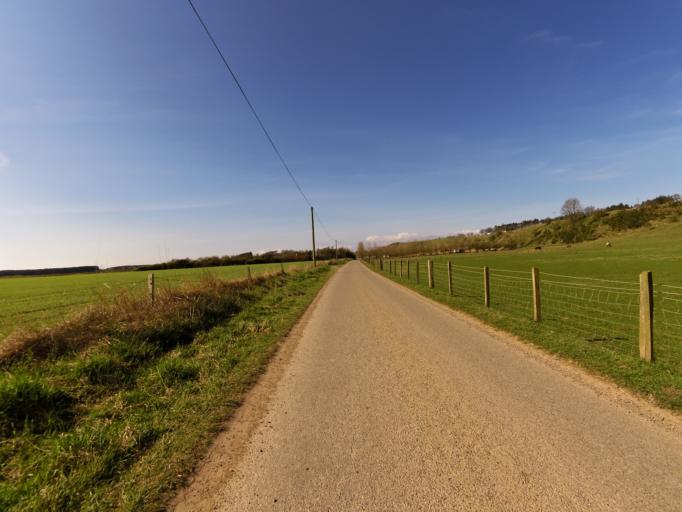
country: GB
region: Scotland
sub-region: Angus
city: Montrose
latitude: 56.7590
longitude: -2.4362
